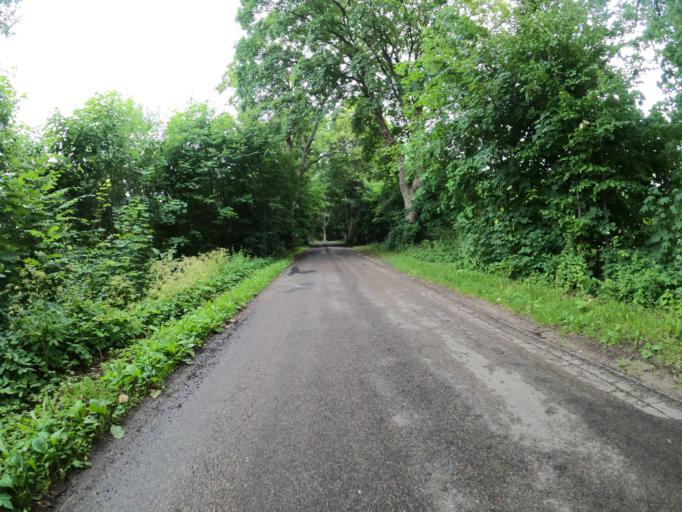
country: PL
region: West Pomeranian Voivodeship
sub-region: Powiat szczecinecki
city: Grzmiaca
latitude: 53.9318
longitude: 16.4584
